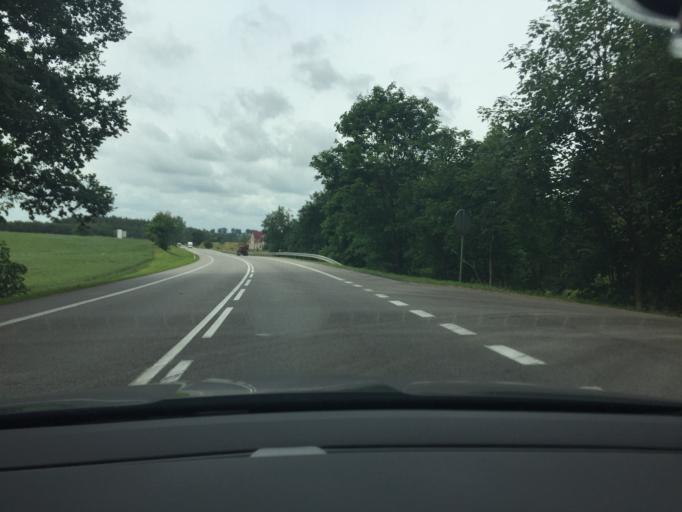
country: PL
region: Pomeranian Voivodeship
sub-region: Powiat starogardzki
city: Smetowo Graniczne
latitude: 53.7429
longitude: 18.7463
